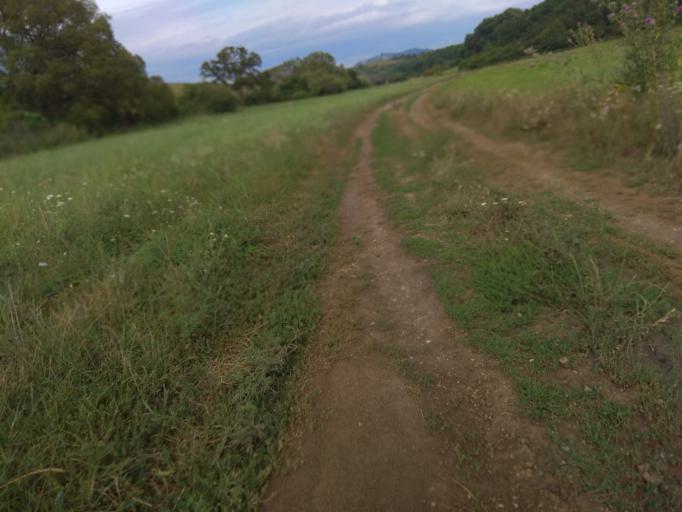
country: HU
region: Heves
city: Belapatfalva
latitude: 48.0188
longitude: 20.2957
